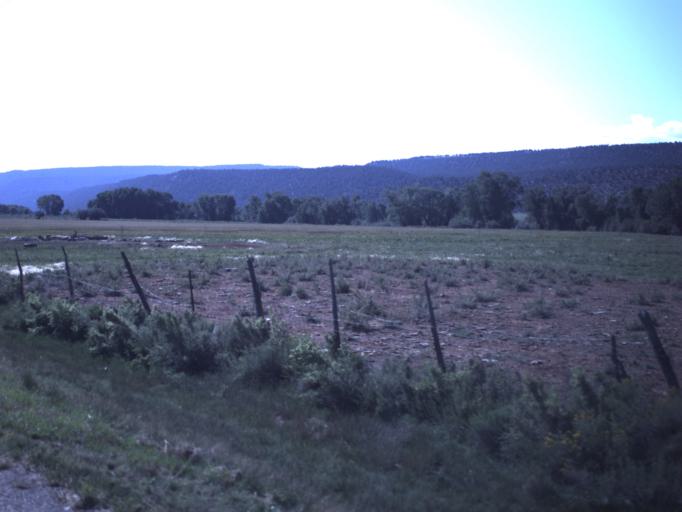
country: US
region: Utah
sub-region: Duchesne County
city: Duchesne
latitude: 40.3379
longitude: -110.6850
